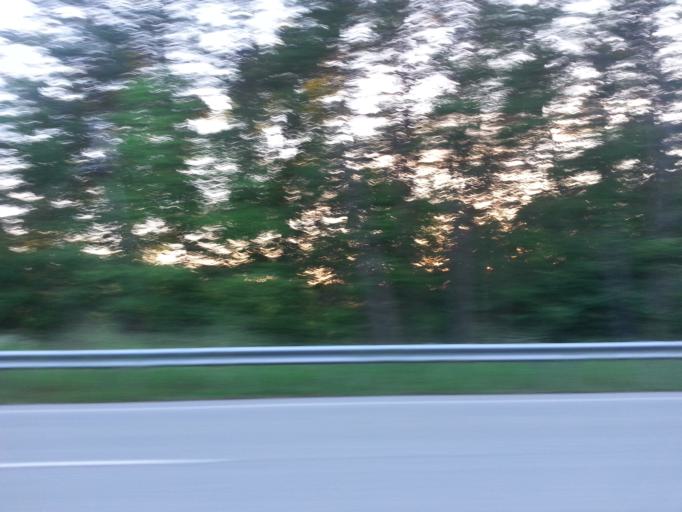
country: US
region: Tennessee
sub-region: Monroe County
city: Madisonville
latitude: 35.3329
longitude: -84.2957
